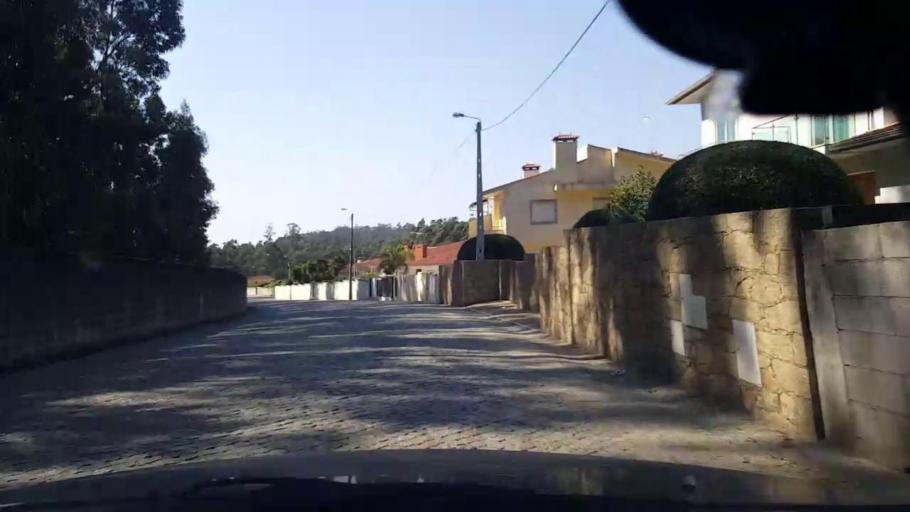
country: PT
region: Porto
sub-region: Povoa de Varzim
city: Pedroso
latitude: 41.4035
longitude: -8.7054
